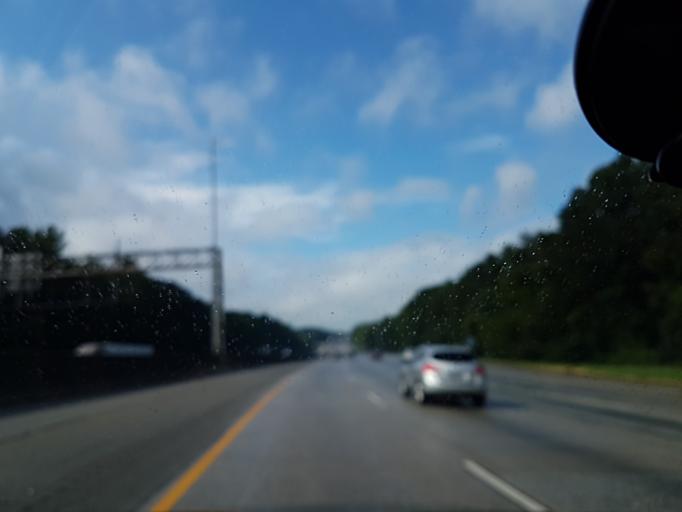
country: US
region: Georgia
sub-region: Fulton County
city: Union City
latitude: 33.6028
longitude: -84.4873
